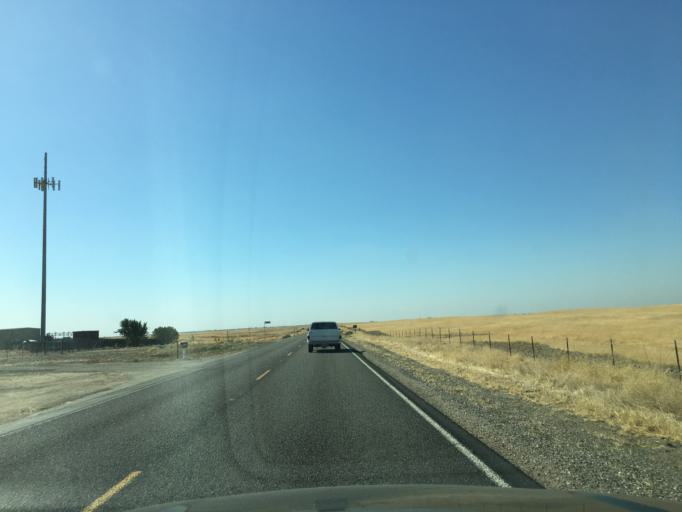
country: US
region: California
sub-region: Madera County
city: Bonadelle Ranchos-Madera Ranchos
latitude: 37.0103
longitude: -119.8902
